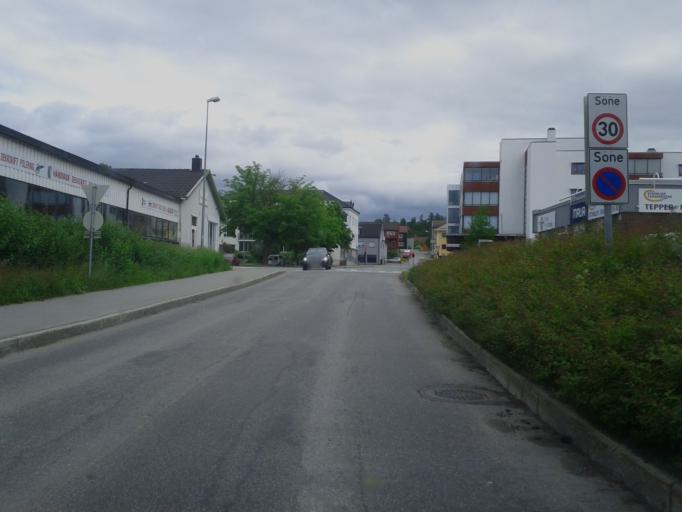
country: NO
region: Nord-Trondelag
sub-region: Steinkjer
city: Steinkjer
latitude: 64.0186
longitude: 11.4930
